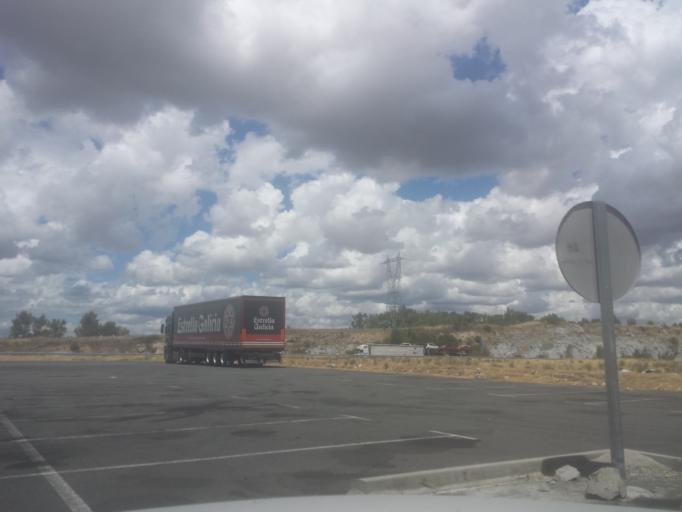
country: ES
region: Castille and Leon
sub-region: Provincia de Salamanca
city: Cantagallo
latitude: 40.3766
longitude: -5.8204
